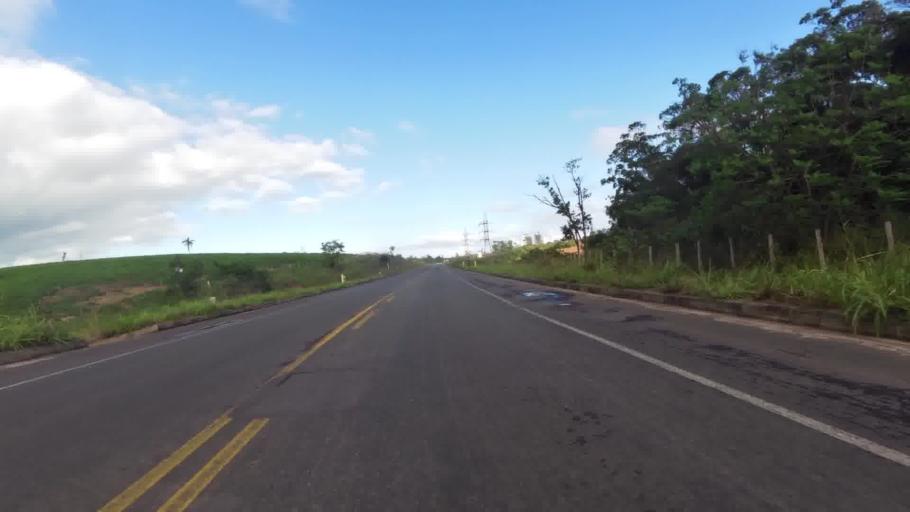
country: BR
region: Espirito Santo
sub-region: Piuma
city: Piuma
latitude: -20.7954
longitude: -40.6152
